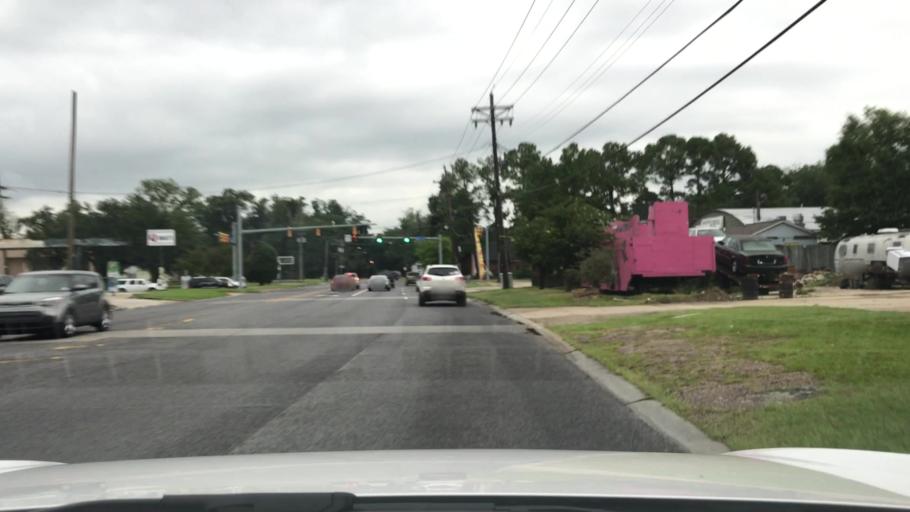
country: US
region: Louisiana
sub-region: East Baton Rouge Parish
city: Baton Rouge
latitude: 30.4530
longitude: -91.1390
